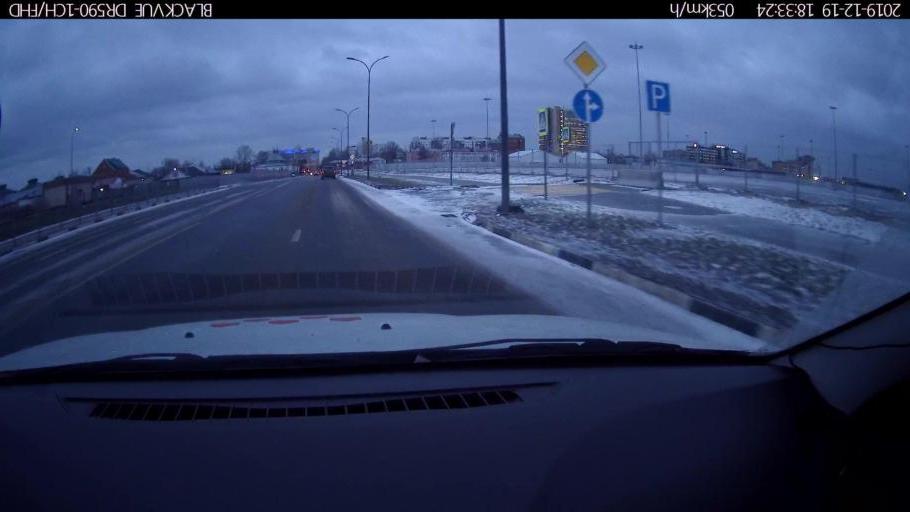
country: RU
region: Nizjnij Novgorod
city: Nizhniy Novgorod
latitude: 56.3345
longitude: 43.9691
